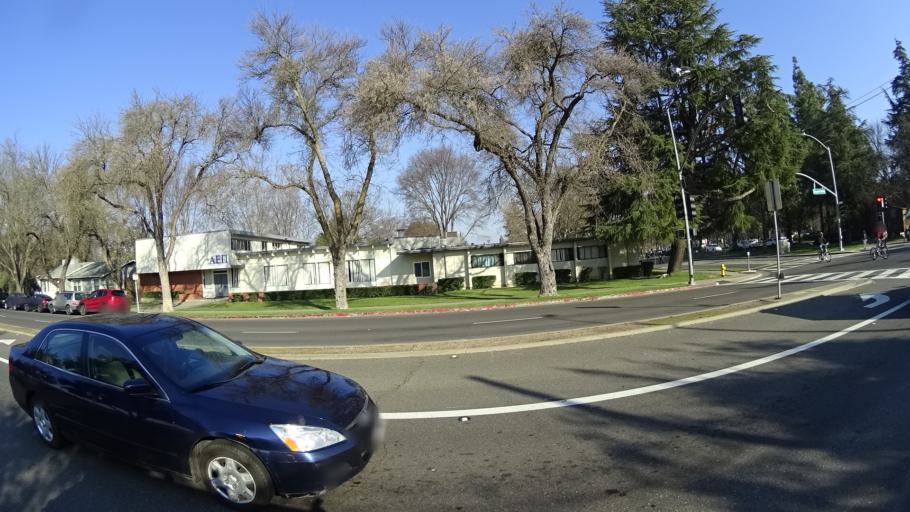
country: US
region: California
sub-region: Yolo County
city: Davis
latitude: 38.5461
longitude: -121.7480
